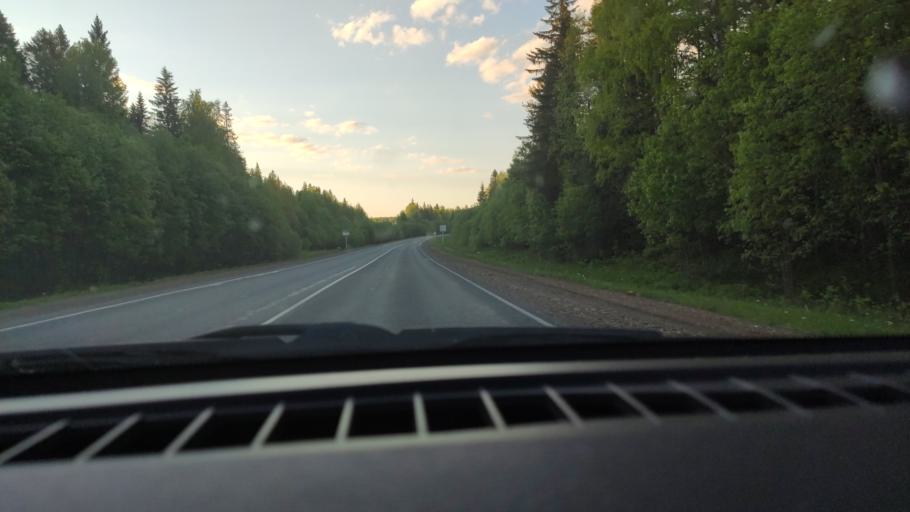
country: RU
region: Perm
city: Dobryanka
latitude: 58.5846
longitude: 56.6525
